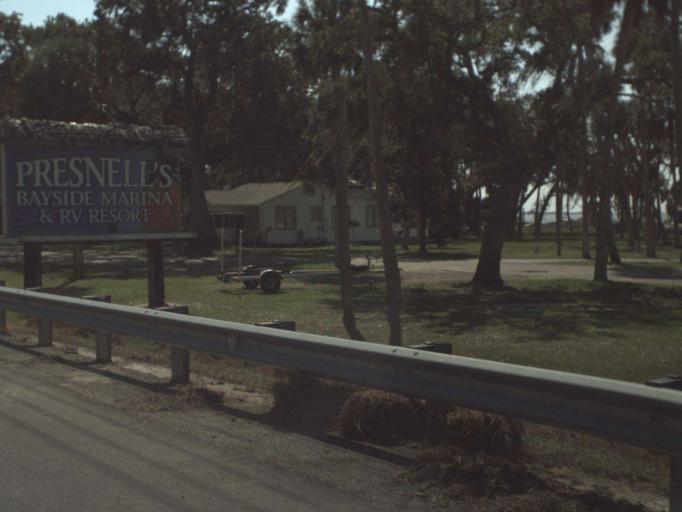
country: US
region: Florida
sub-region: Gulf County
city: Port Saint Joe
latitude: 29.7478
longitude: -85.3029
